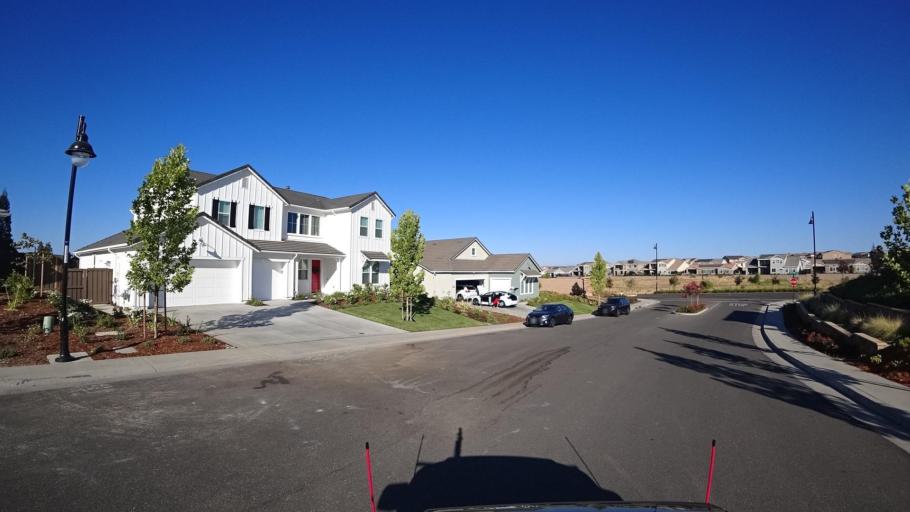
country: US
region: California
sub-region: Placer County
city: Rocklin
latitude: 38.8255
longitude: -121.2672
